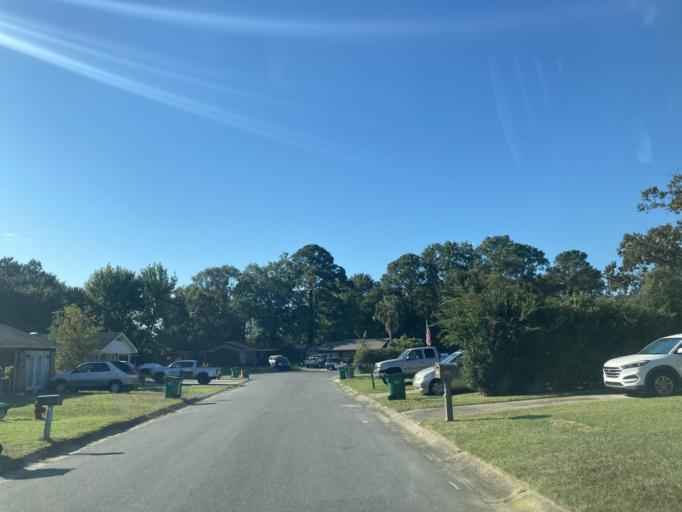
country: US
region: Mississippi
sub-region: Jackson County
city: Saint Martin
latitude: 30.4456
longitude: -88.8828
